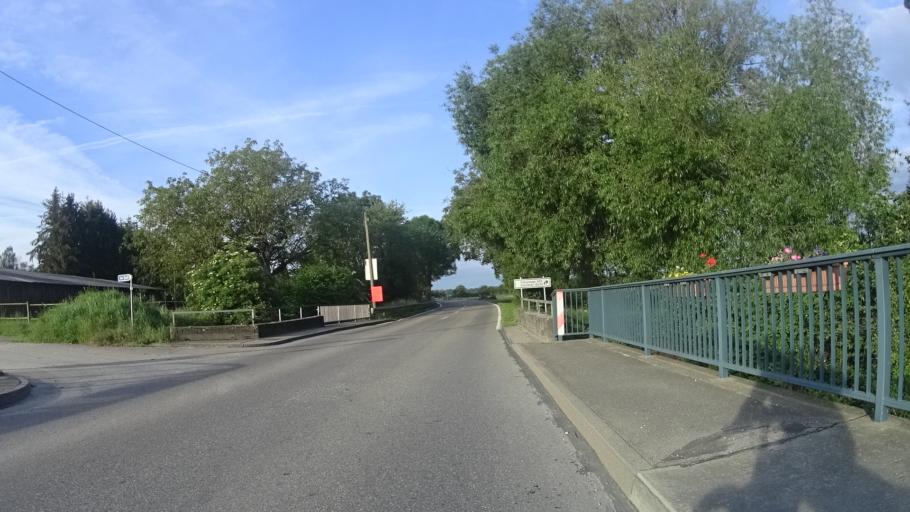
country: DE
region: Baden-Wuerttemberg
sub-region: Freiburg Region
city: Hartheim
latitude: 47.9668
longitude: 7.6442
